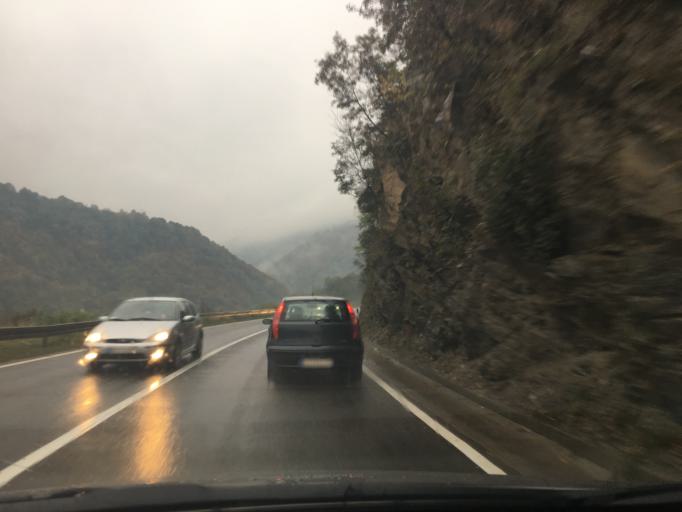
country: RS
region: Central Serbia
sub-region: Pcinjski Okrug
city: Vladicin Han
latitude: 42.7353
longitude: 22.0594
